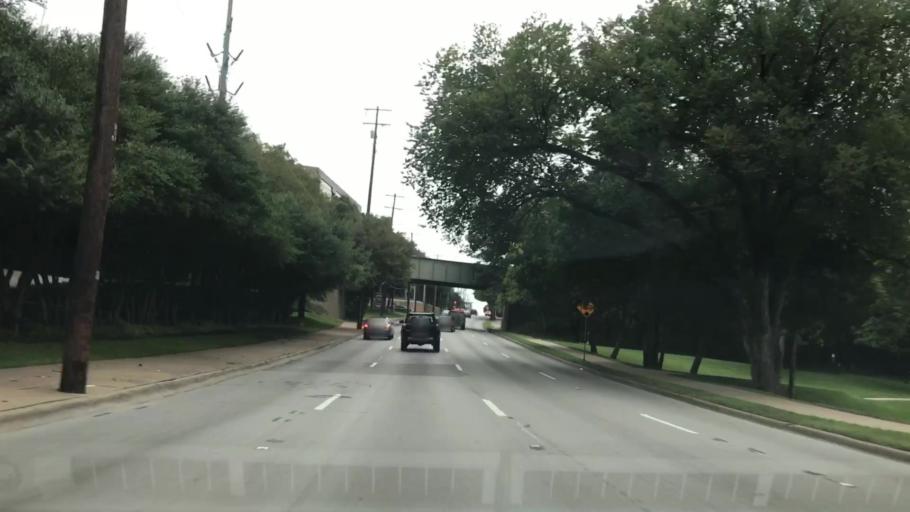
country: US
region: Texas
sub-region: Dallas County
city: Dallas
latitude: 32.8090
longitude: -96.8022
